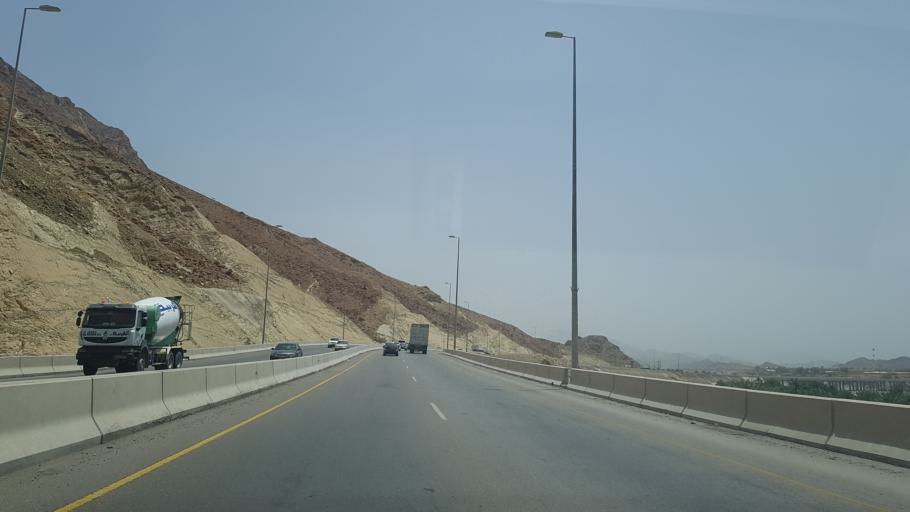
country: OM
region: Muhafazat ad Dakhiliyah
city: Bidbid
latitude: 23.4532
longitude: 58.1196
